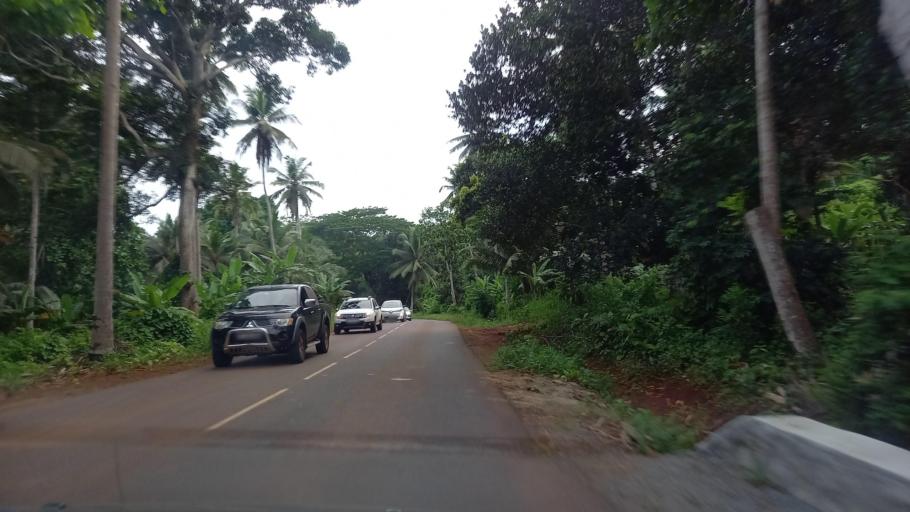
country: YT
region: M'Tsangamouji
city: M'Tsangamouji
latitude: -12.7577
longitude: 45.0960
